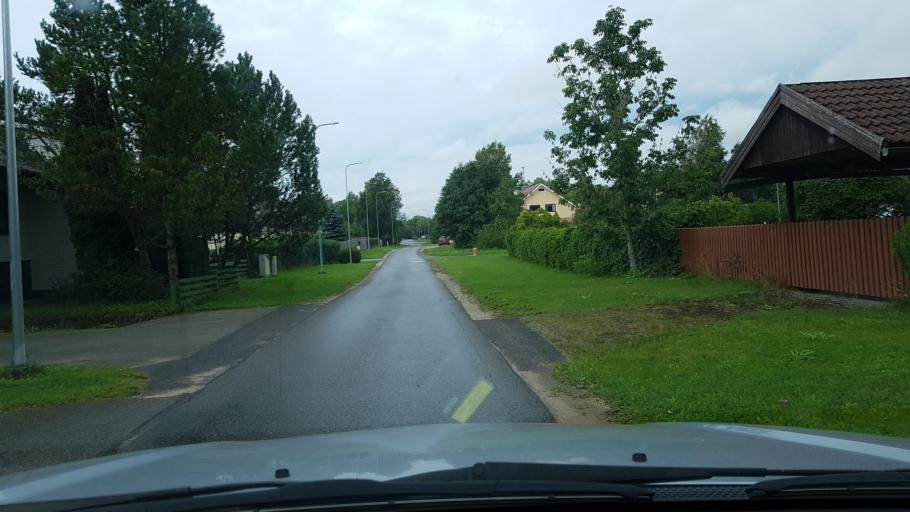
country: EE
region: Harju
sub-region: Rae vald
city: Jueri
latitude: 59.3546
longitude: 24.9211
